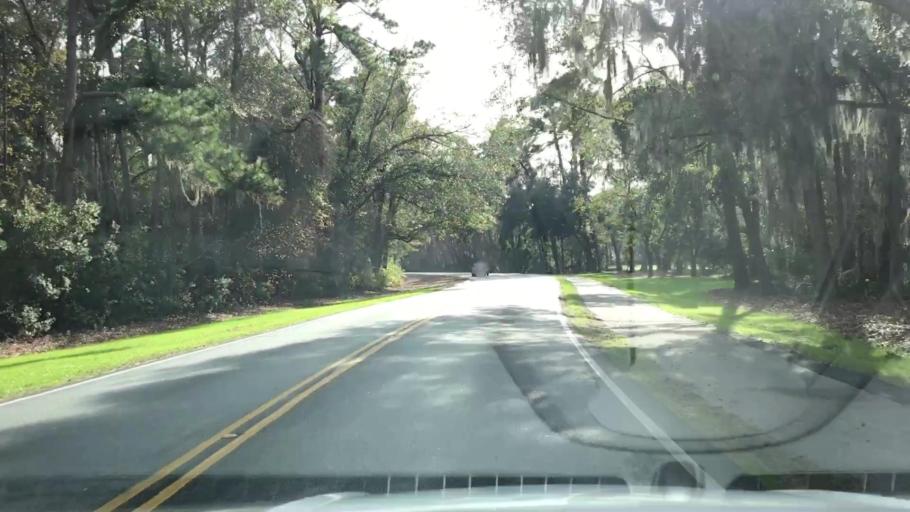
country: US
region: South Carolina
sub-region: Beaufort County
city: Hilton Head Island
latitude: 32.2214
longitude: -80.7234
